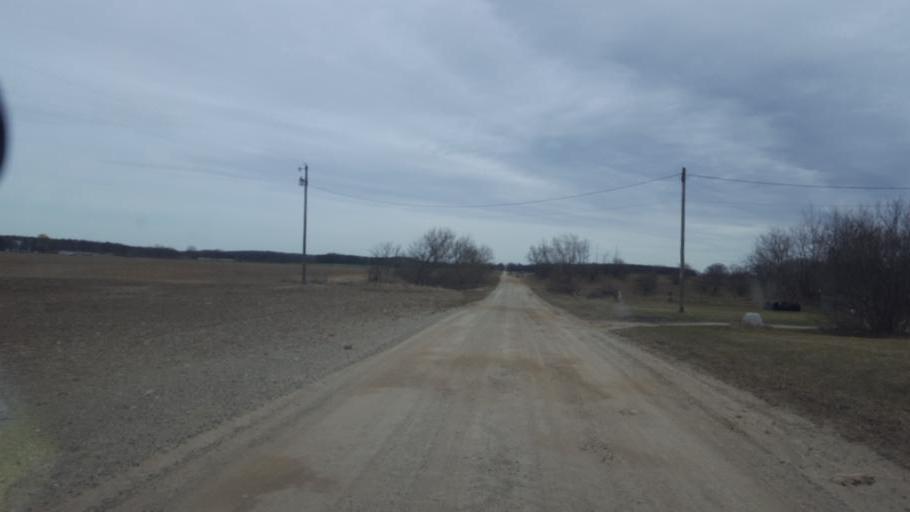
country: US
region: Michigan
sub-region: Montcalm County
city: Edmore
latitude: 43.4513
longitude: -85.0127
